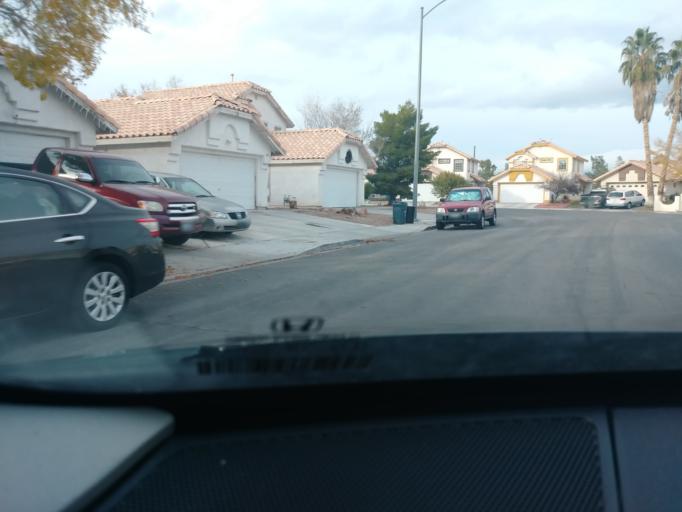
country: US
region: Nevada
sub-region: Clark County
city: Spring Valley
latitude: 36.1801
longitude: -115.2156
